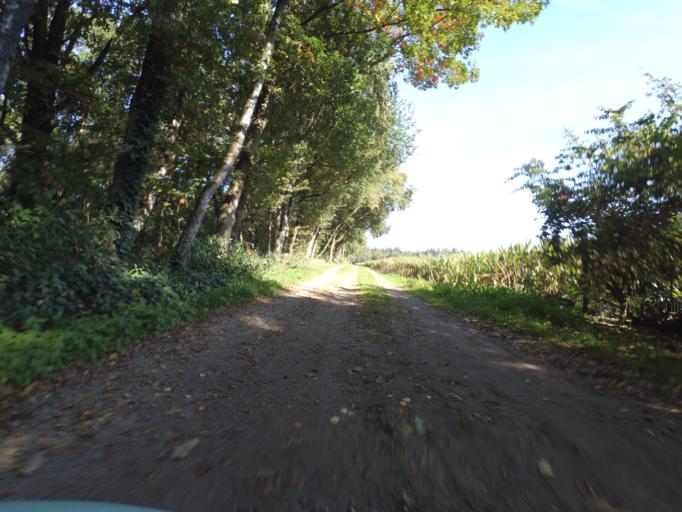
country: NL
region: Gelderland
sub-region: Gemeente Lochem
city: Almen
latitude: 52.1125
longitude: 6.3504
